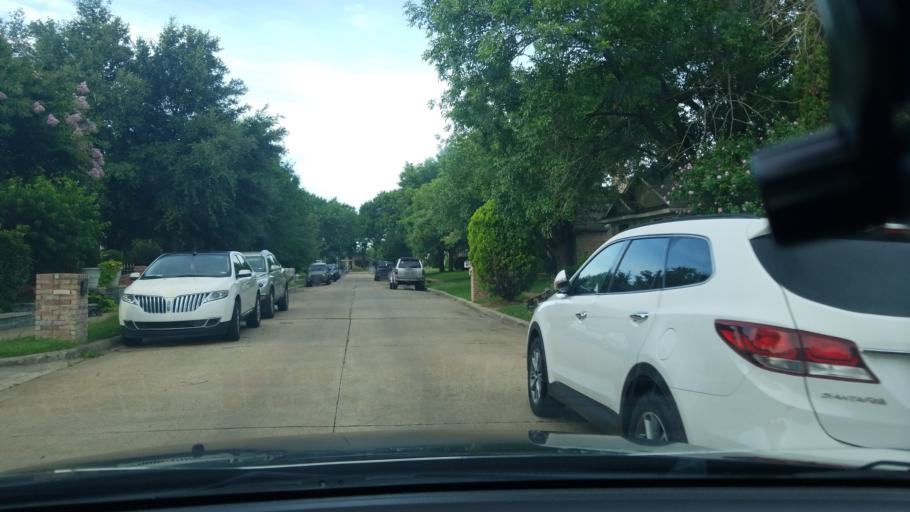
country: US
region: Texas
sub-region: Dallas County
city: Balch Springs
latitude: 32.7530
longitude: -96.6424
